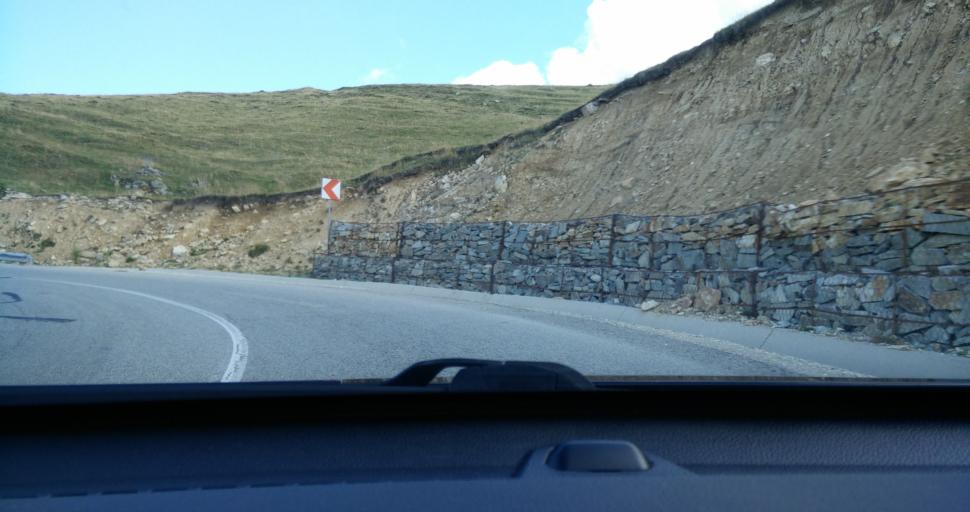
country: RO
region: Gorj
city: Novaci-Straini
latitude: 45.2455
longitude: 23.6953
